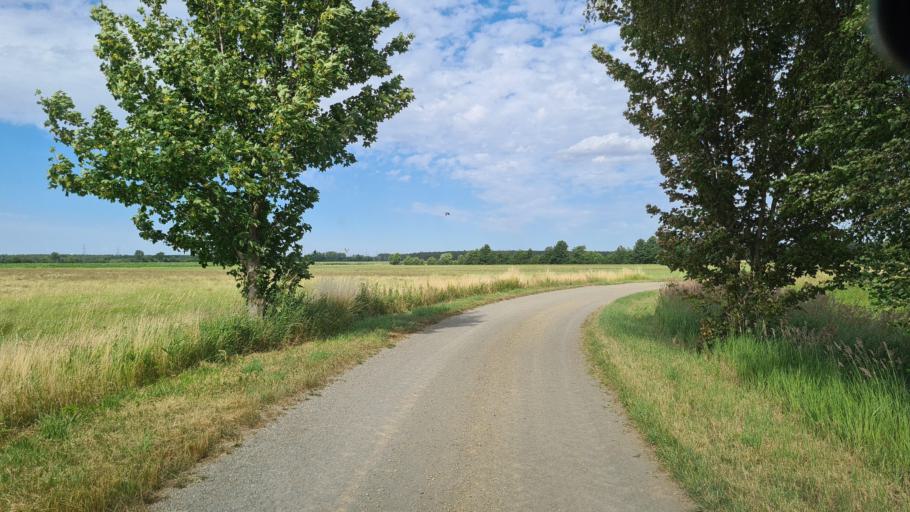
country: DE
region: Saxony-Anhalt
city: Holzdorf
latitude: 51.8149
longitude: 13.1826
